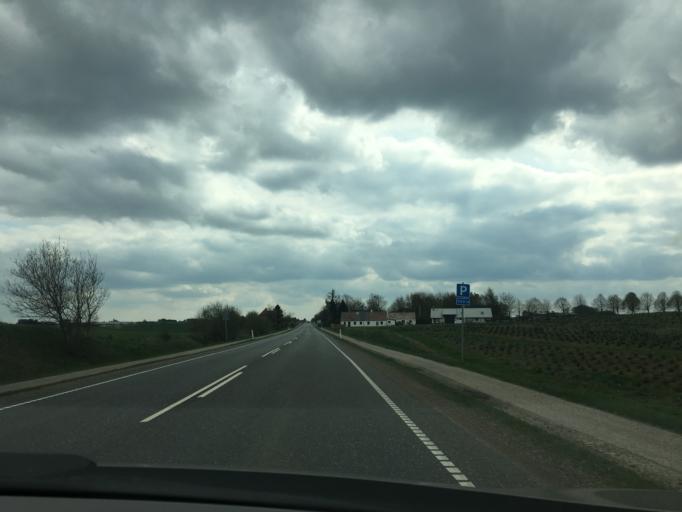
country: DK
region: Central Jutland
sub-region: Horsens Kommune
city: Braedstrup
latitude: 56.0051
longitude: 9.6046
